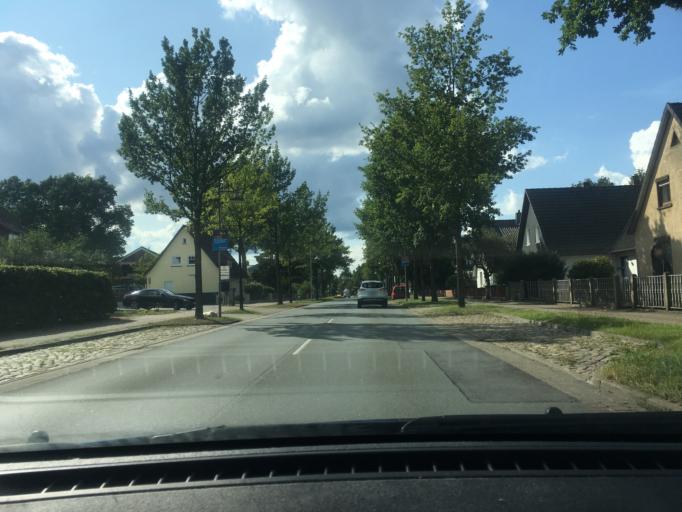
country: DE
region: Lower Saxony
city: Soltau
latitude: 52.9871
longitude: 9.8711
